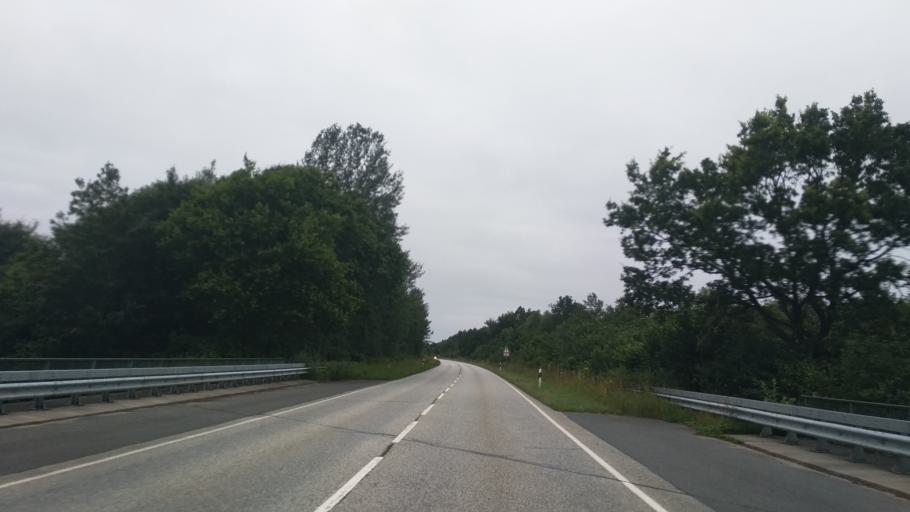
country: DE
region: Schleswig-Holstein
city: Lurschau
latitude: 54.5341
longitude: 9.5093
